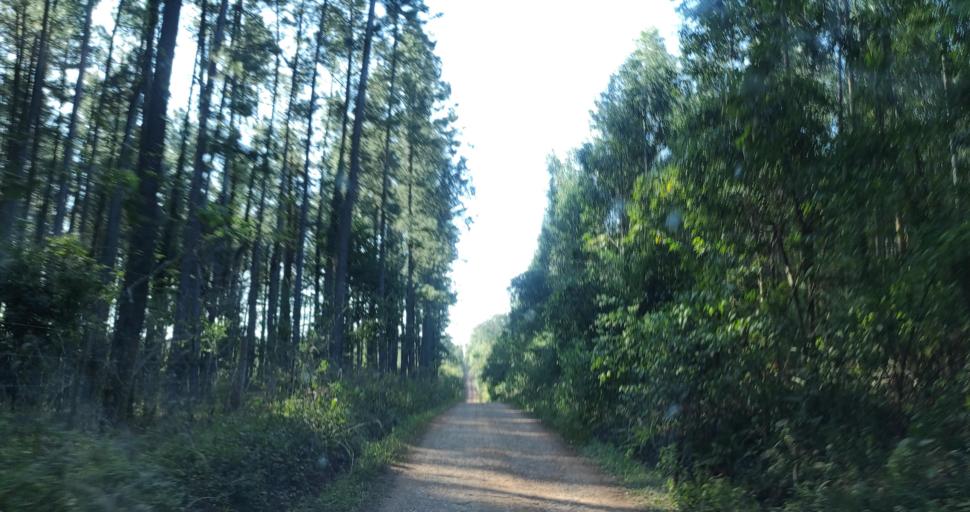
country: AR
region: Misiones
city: Capiovi
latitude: -26.8866
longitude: -55.1075
